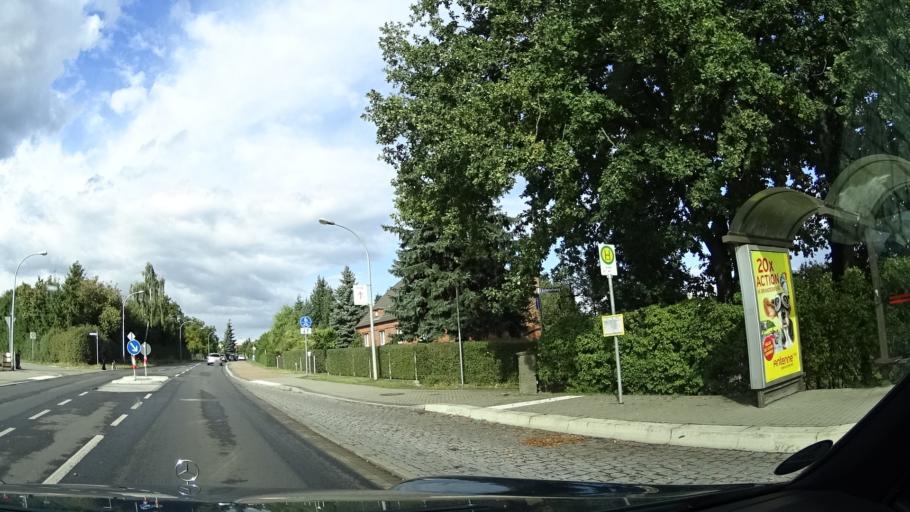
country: DE
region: Brandenburg
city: Neuruppin
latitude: 52.8941
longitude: 12.7981
